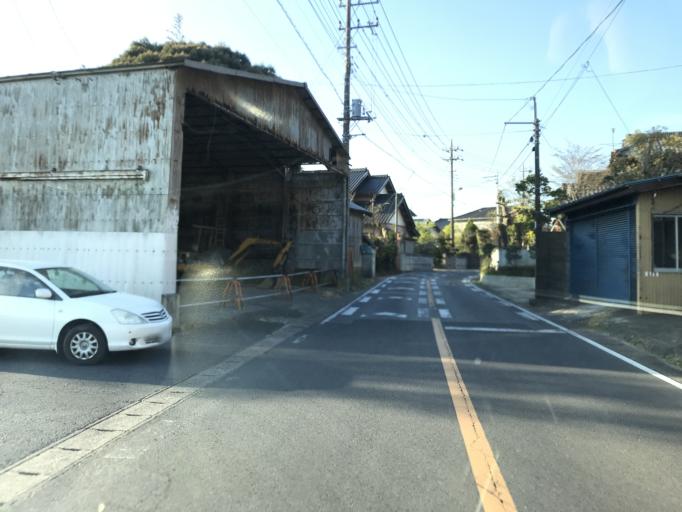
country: JP
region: Chiba
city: Yokaichiba
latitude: 35.7155
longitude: 140.5648
